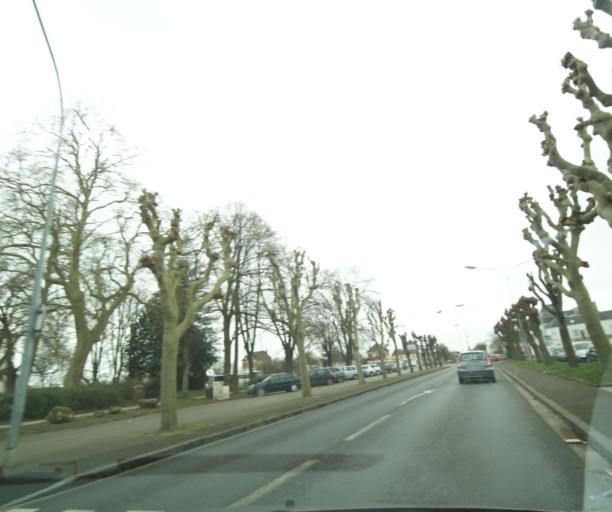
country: FR
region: Picardie
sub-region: Departement de l'Oise
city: Noyon
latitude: 49.5791
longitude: 3.0062
